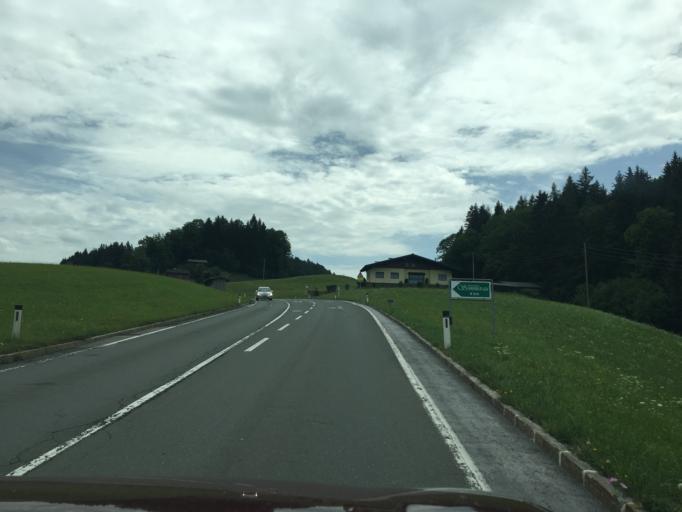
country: AT
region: Salzburg
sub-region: Politischer Bezirk Hallein
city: Adnet
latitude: 47.6610
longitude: 13.1688
